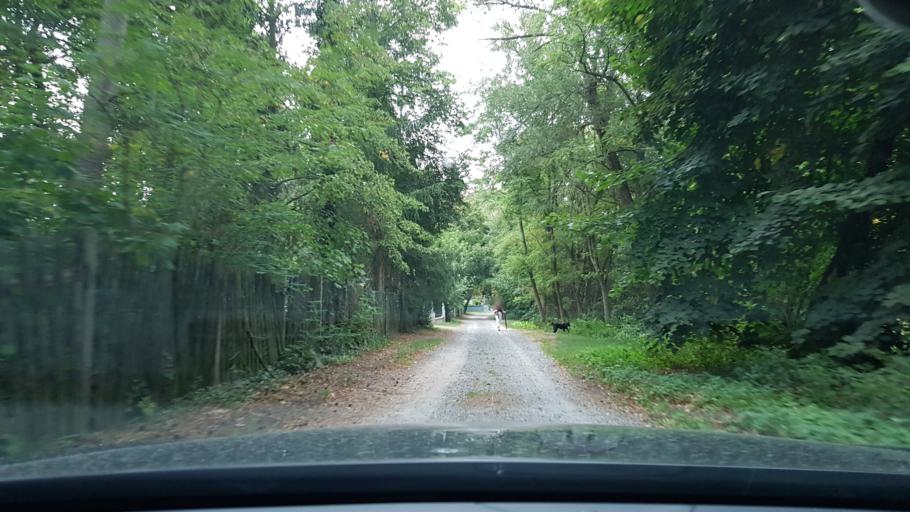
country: DE
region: Berlin
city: Mahlsdorf
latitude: 52.4823
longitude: 13.6297
